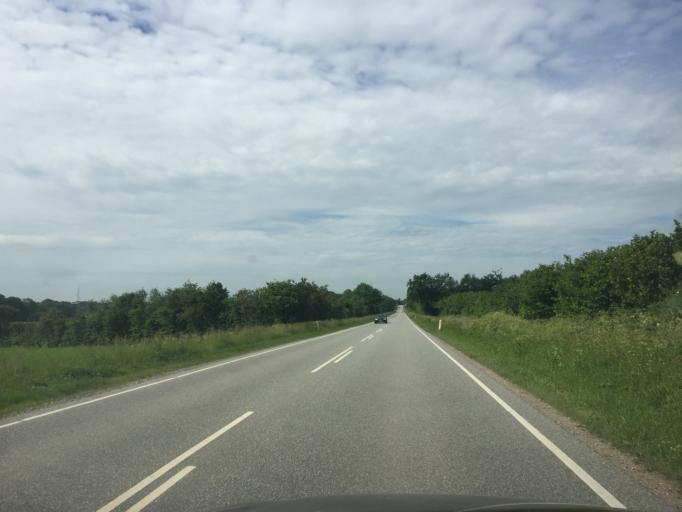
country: DK
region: South Denmark
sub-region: Kerteminde Kommune
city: Langeskov
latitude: 55.2257
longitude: 10.6244
